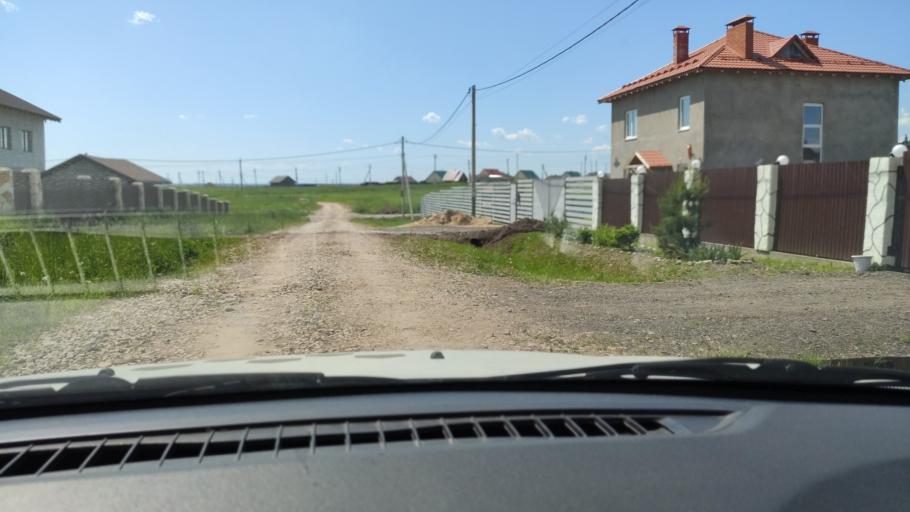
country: RU
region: Perm
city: Ferma
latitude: 57.9423
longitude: 56.3406
